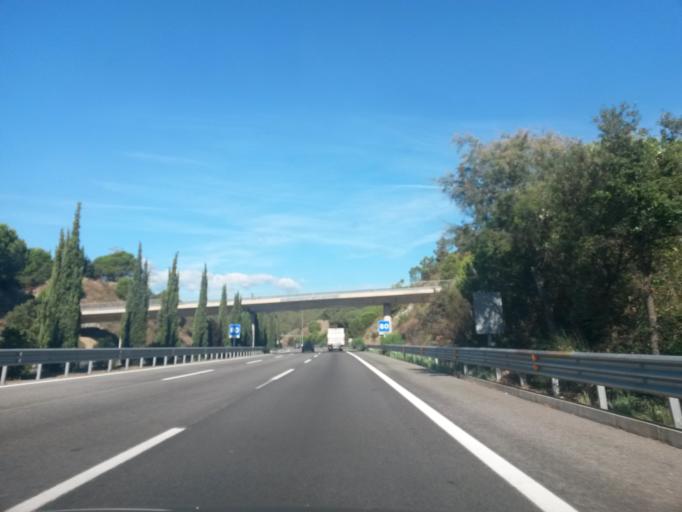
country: ES
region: Catalonia
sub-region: Provincia de Barcelona
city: Canet de Mar
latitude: 41.5999
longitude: 2.5840
